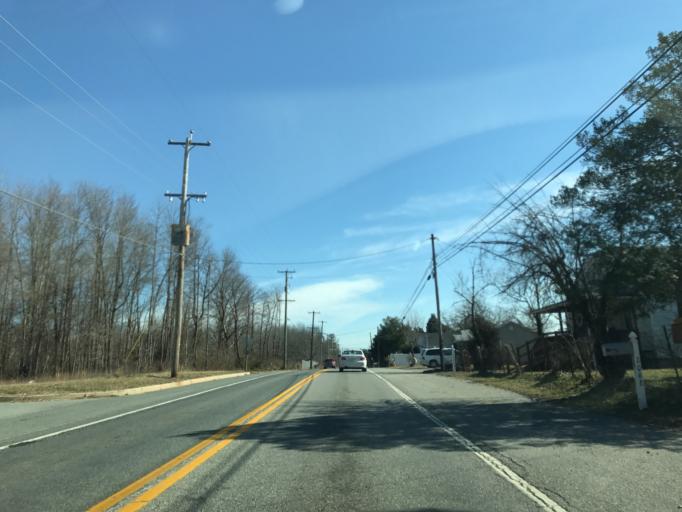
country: US
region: Maryland
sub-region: Cecil County
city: Elkton
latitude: 39.6057
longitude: -75.8634
